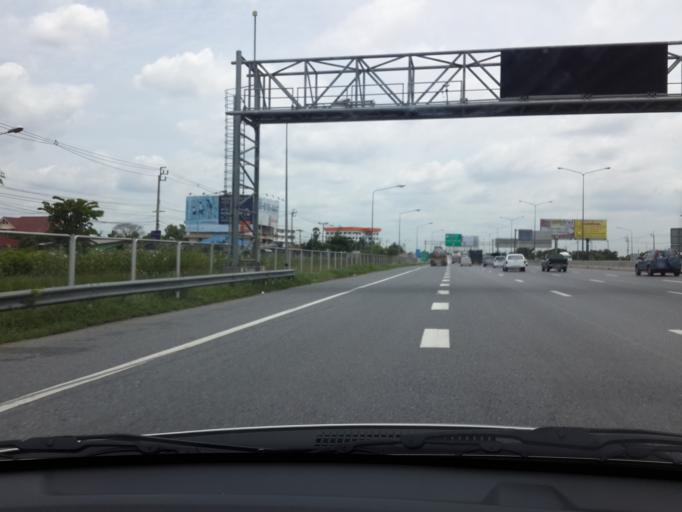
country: TH
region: Bangkok
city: Saphan Sung
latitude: 13.7435
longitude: 100.7025
